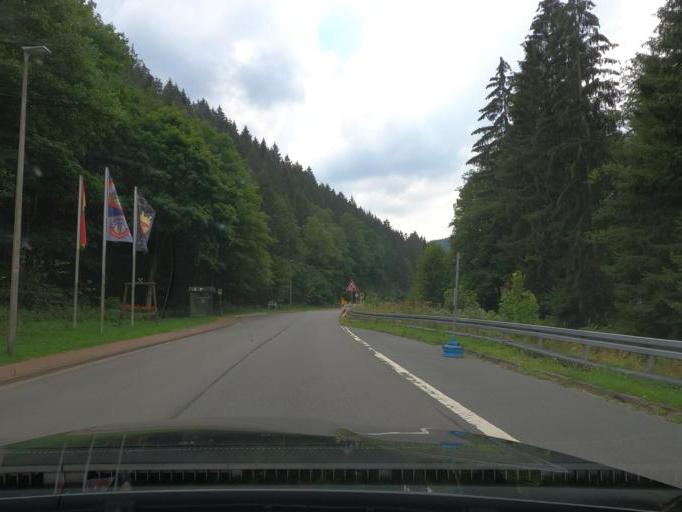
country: DE
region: Lower Saxony
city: Wildemann
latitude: 51.8618
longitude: 10.2804
